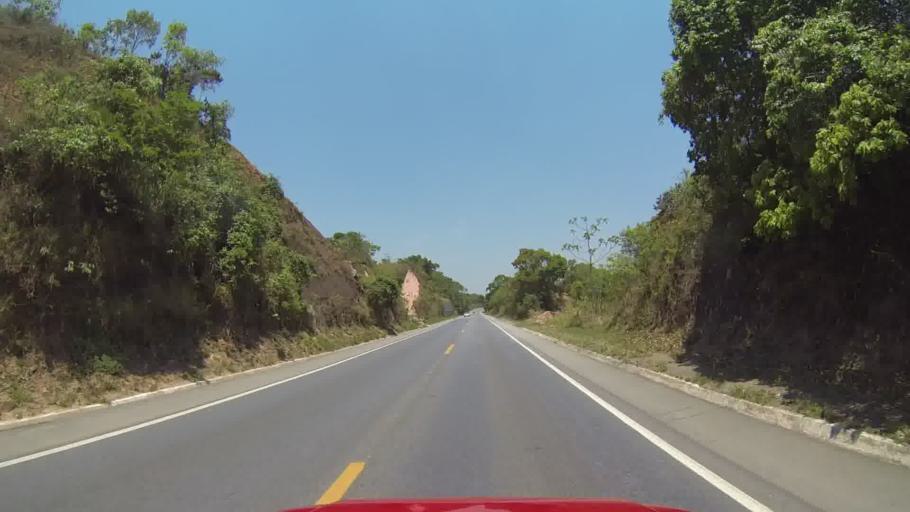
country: BR
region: Minas Gerais
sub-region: Itapecerica
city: Itapecerica
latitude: -20.3215
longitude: -45.2207
